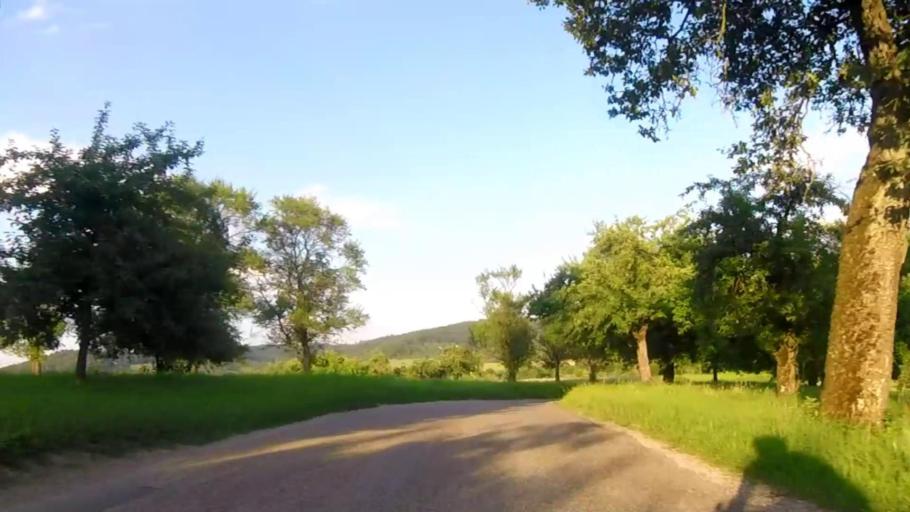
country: DE
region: Baden-Wuerttemberg
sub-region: Regierungsbezirk Stuttgart
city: Oppenweiler
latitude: 48.9738
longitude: 9.4531
